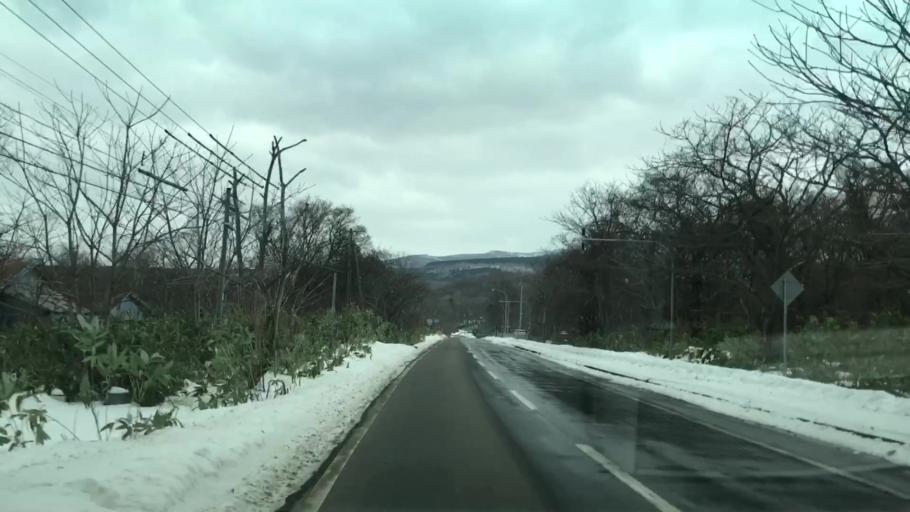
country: JP
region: Hokkaido
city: Yoichi
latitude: 43.3352
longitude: 140.4650
